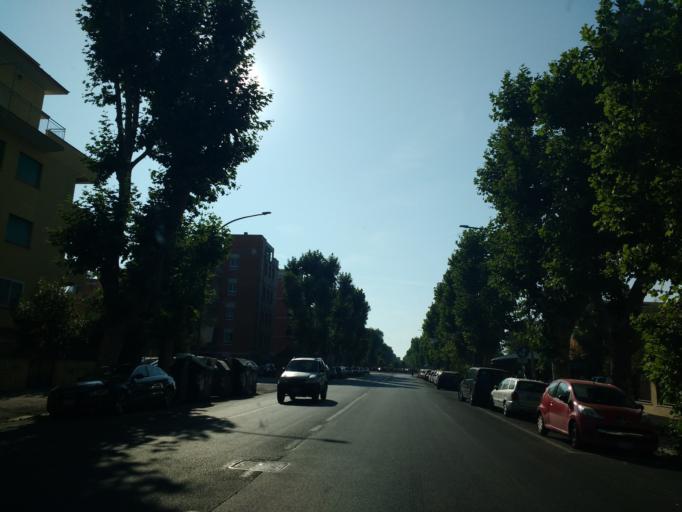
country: IT
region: Latium
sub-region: Citta metropolitana di Roma Capitale
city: Lido di Ostia
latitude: 41.7269
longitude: 12.2887
